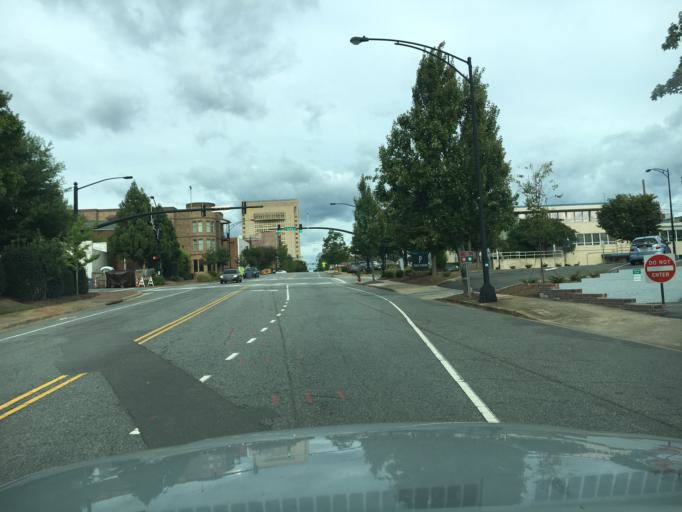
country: US
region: South Carolina
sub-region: Spartanburg County
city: Spartanburg
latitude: 34.9483
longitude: -81.9338
